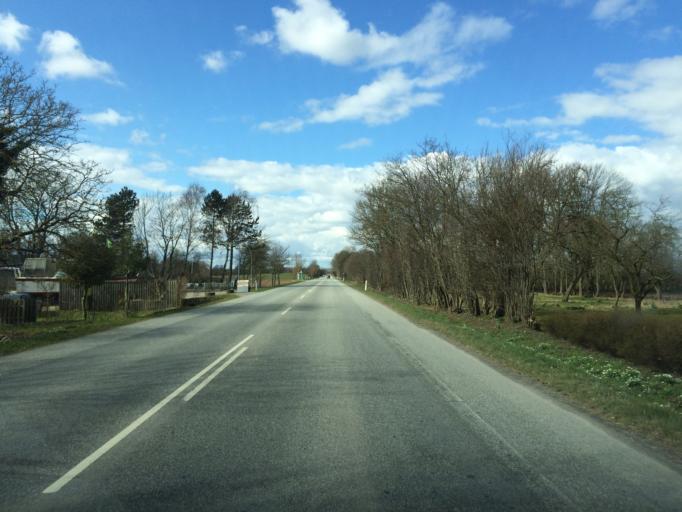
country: DK
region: South Denmark
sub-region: Assens Kommune
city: Arup
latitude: 55.4322
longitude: 10.0102
